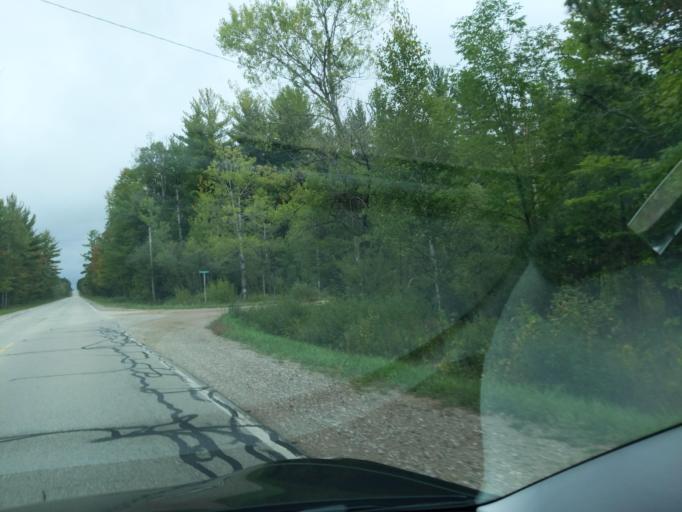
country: US
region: Michigan
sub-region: Grand Traverse County
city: Kingsley
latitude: 44.6126
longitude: -85.3532
